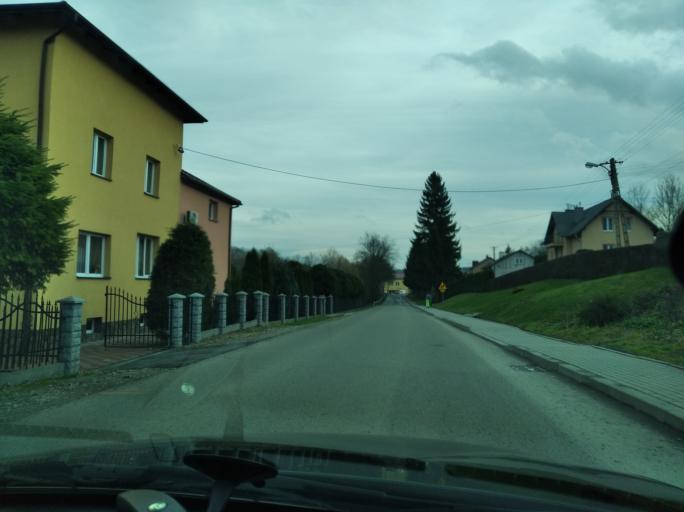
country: PL
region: Subcarpathian Voivodeship
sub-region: Powiat strzyzowski
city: Strzyzow
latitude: 49.9361
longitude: 21.7595
